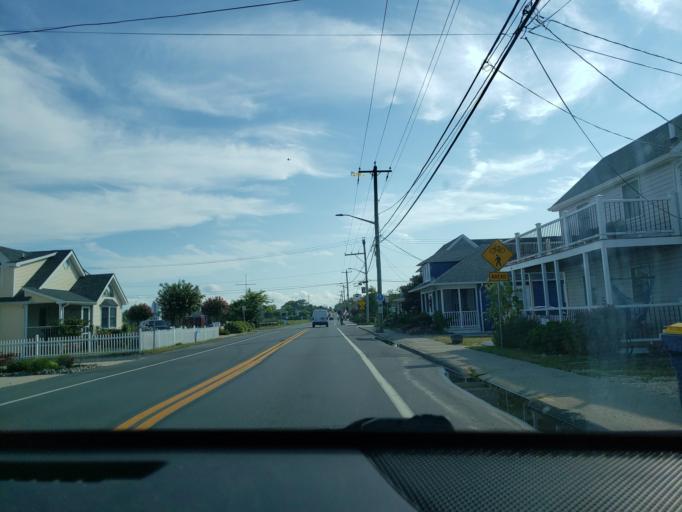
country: US
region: Delaware
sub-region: Sussex County
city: Lewes
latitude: 38.7796
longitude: -75.1336
